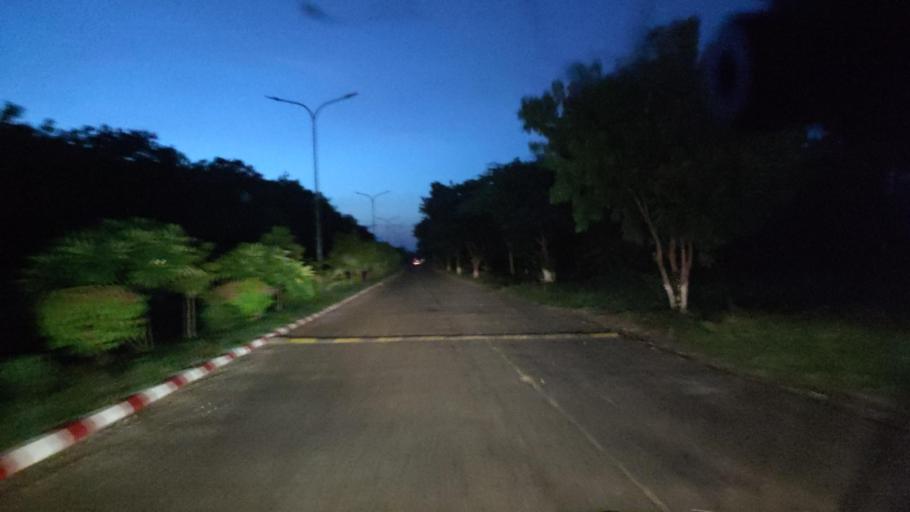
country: MM
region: Magway
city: Pakokku
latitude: 21.1661
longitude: 94.9238
